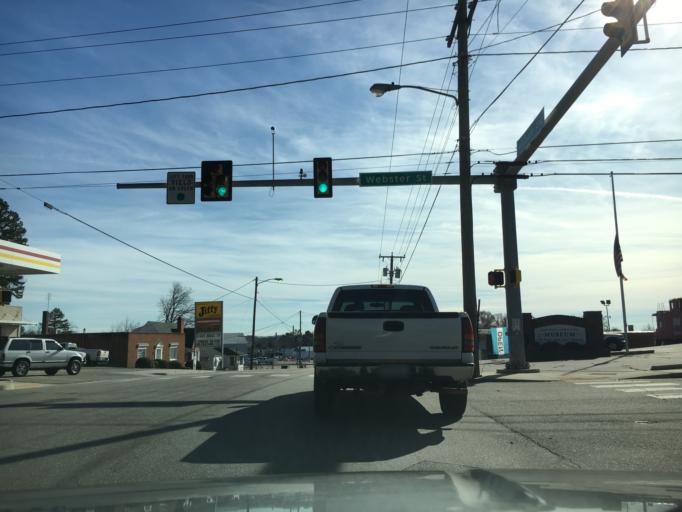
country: US
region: Virginia
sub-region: Halifax County
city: South Boston
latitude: 36.7065
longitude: -78.9101
